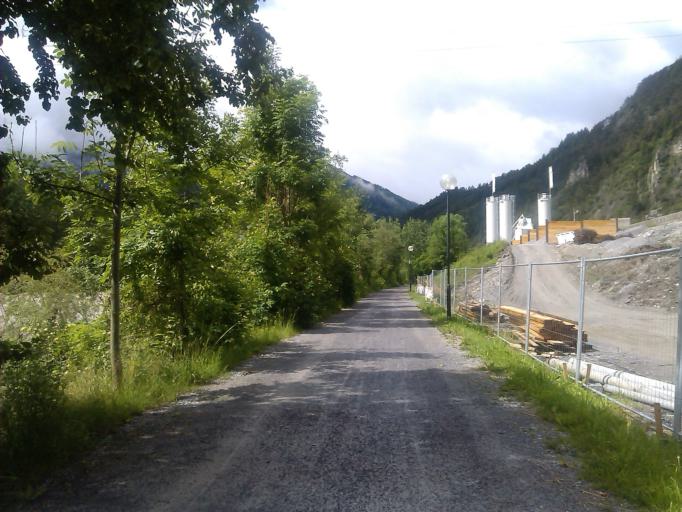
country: AT
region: Tyrol
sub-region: Politischer Bezirk Landeck
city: Zams
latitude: 47.1588
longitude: 10.5772
